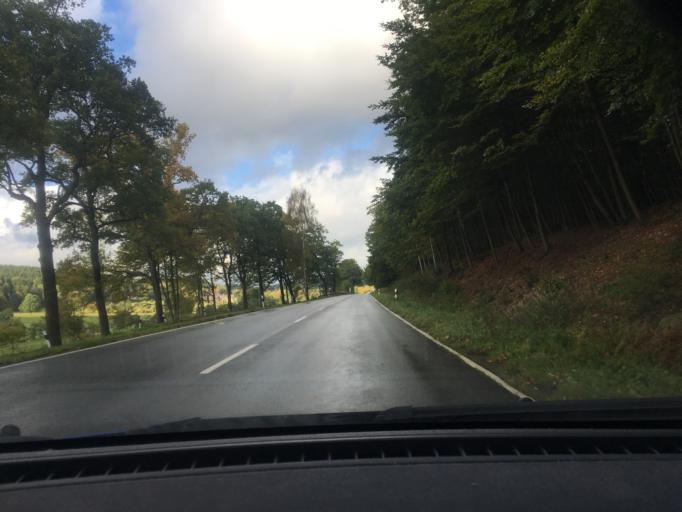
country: DE
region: Lower Saxony
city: Derental
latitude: 51.7390
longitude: 9.5147
